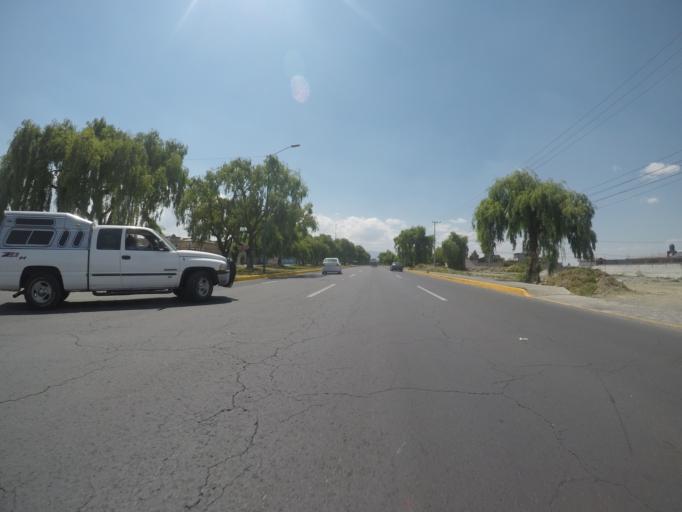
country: MX
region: Mexico
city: Cacalomacan
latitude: 19.2568
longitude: -99.6988
